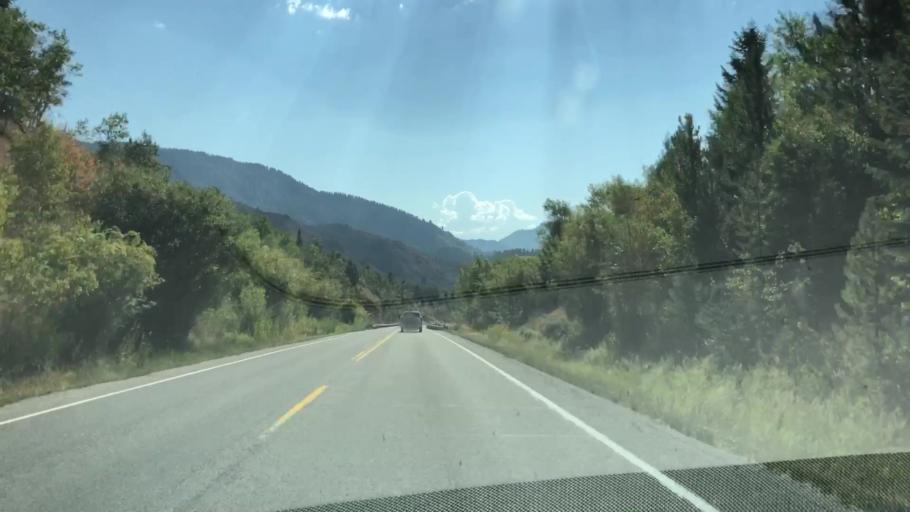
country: US
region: Wyoming
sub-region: Teton County
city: Hoback
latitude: 43.2261
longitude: -111.0821
